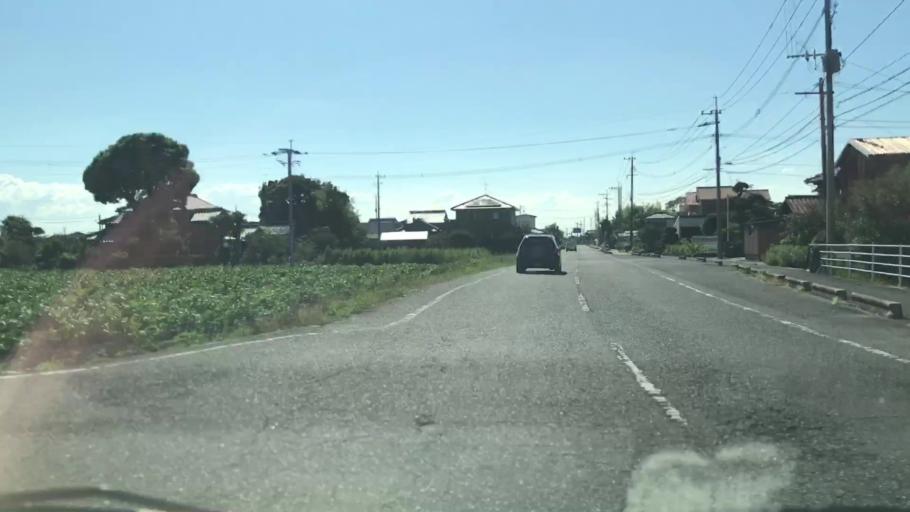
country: JP
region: Saga Prefecture
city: Okawa
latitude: 33.2198
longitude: 130.3403
